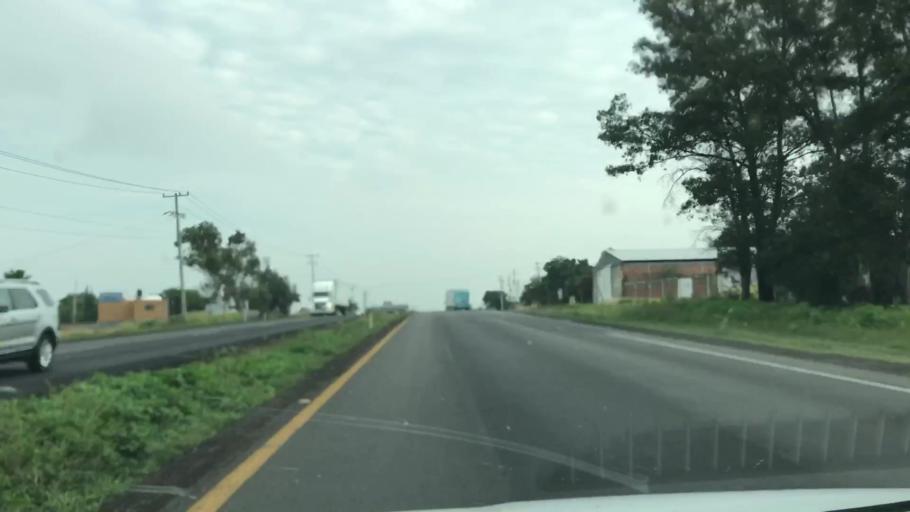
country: MX
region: Guanajuato
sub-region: Irapuato
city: San Ignacio de Rivera (Ojo de Agua)
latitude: 20.5416
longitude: -101.4562
